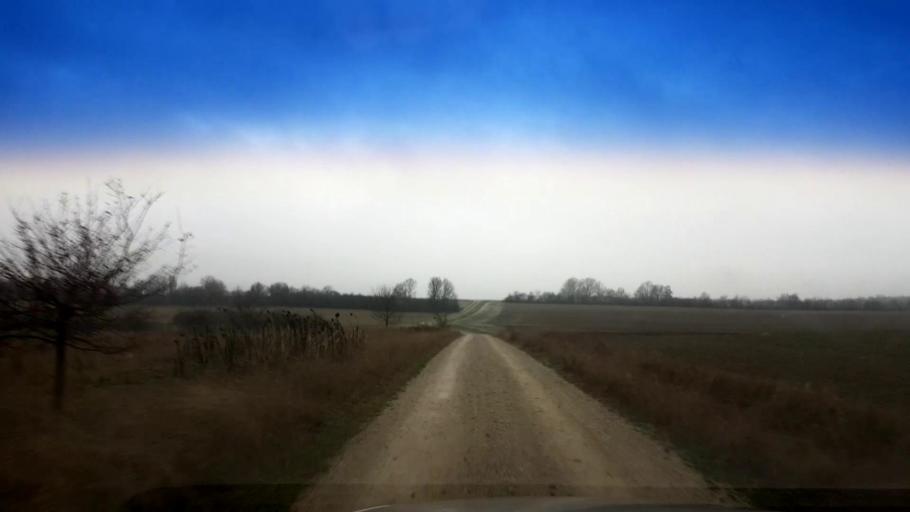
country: DE
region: Bavaria
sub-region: Upper Franconia
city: Schesslitz
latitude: 49.9980
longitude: 11.0400
